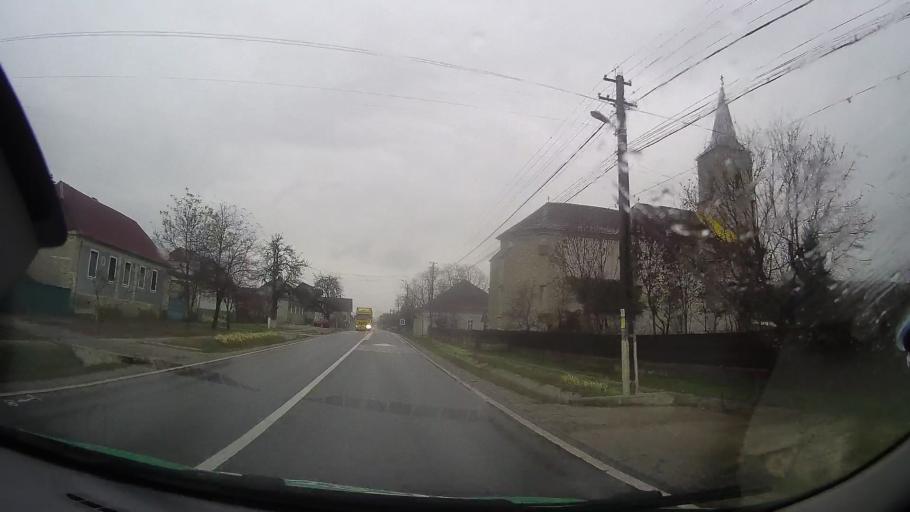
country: RO
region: Bistrita-Nasaud
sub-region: Comuna Galatii Bistritei
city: Galatii Bistritei
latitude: 46.9705
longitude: 24.4335
